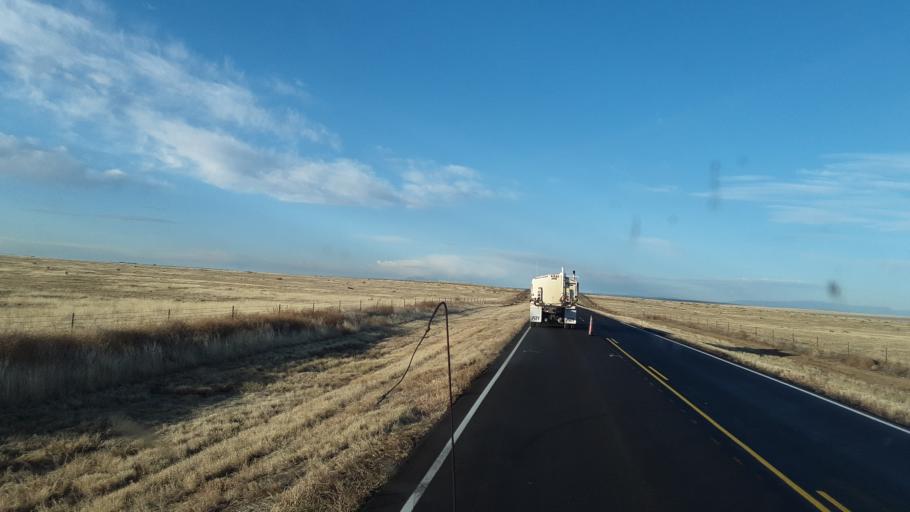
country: US
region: Colorado
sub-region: Otero County
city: Rocky Ford
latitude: 37.9625
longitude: -103.8431
